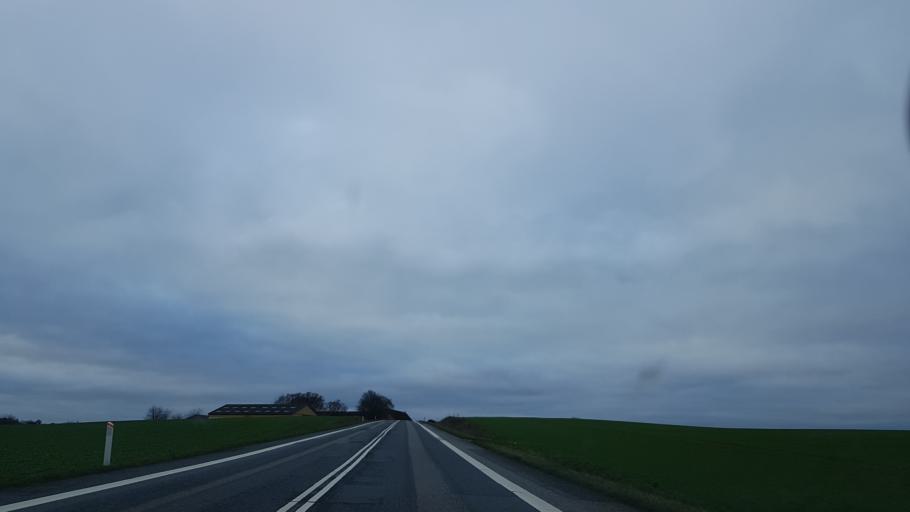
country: DK
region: Zealand
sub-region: Holbaek Kommune
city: Jyderup
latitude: 55.7091
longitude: 11.3739
